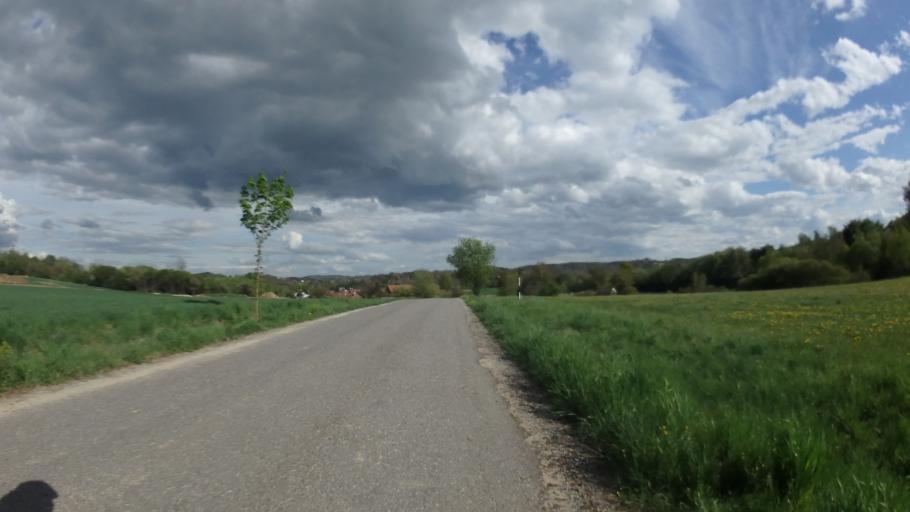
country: CZ
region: Vysocina
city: Merin
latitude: 49.3404
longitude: 15.8938
